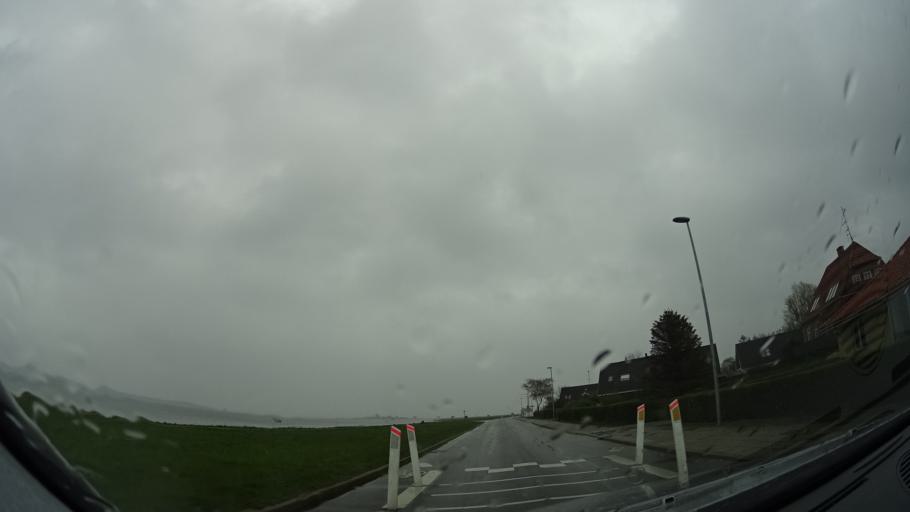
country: DK
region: Zealand
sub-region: Holbaek Kommune
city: Holbaek
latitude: 55.7211
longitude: 11.7420
